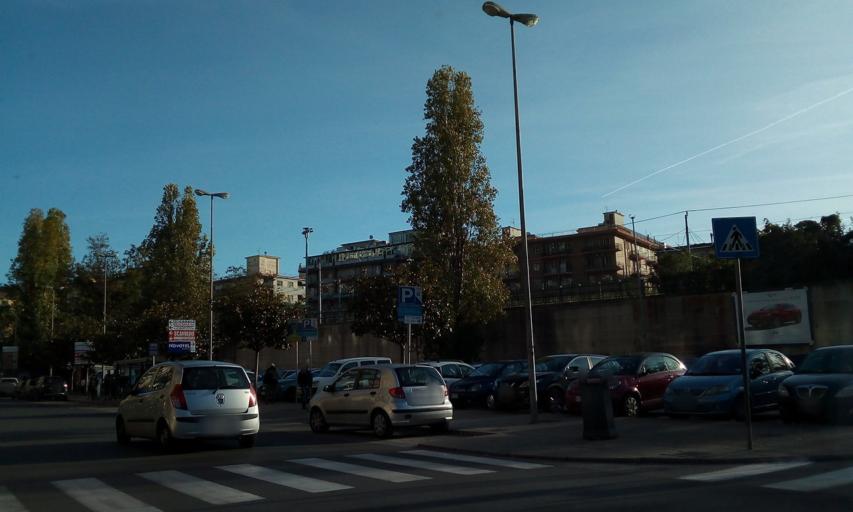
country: IT
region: Campania
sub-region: Provincia di Salerno
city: Salerno
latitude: 40.6741
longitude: 14.7768
